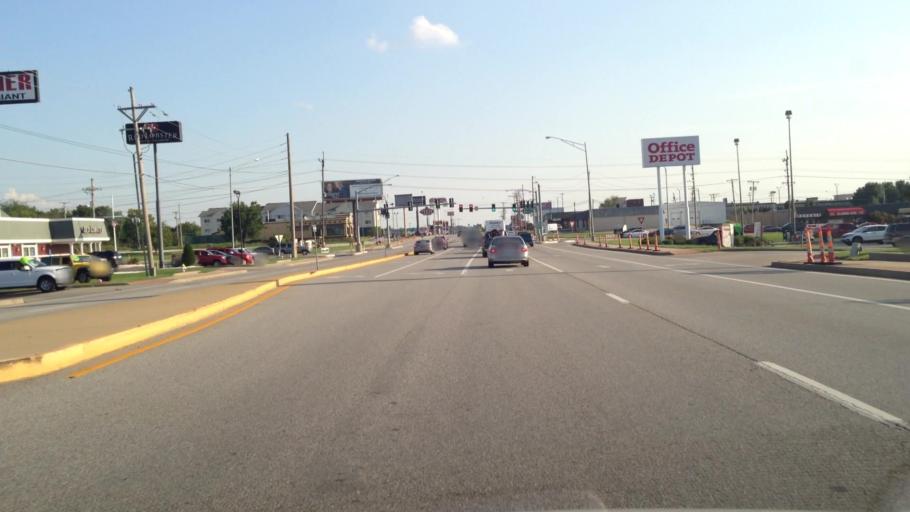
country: US
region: Missouri
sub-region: Jasper County
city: Duquesne
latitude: 37.0564
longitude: -94.4783
